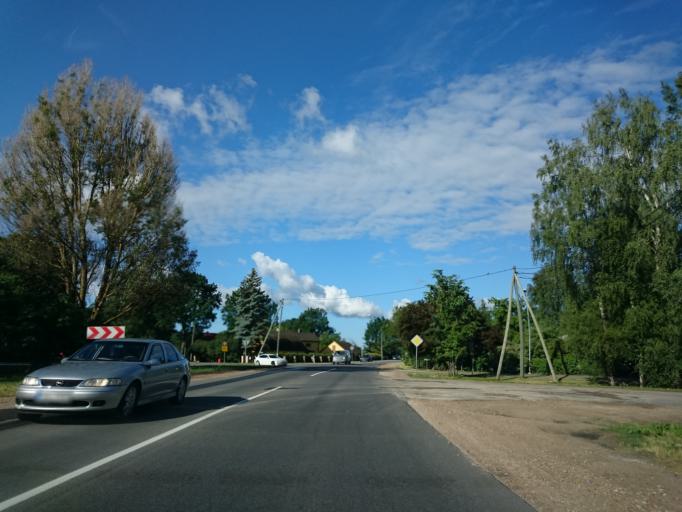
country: LV
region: Marupe
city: Marupe
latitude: 56.9010
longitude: 24.0482
